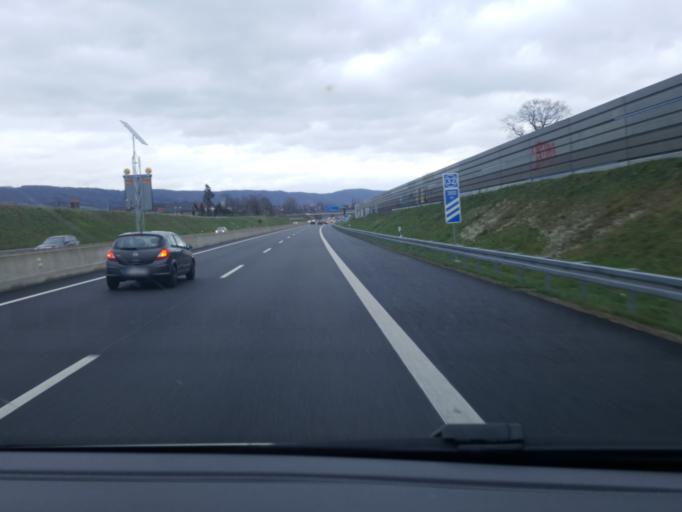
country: DE
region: North Rhine-Westphalia
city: Bad Oeynhausen
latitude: 52.2303
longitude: 8.7834
